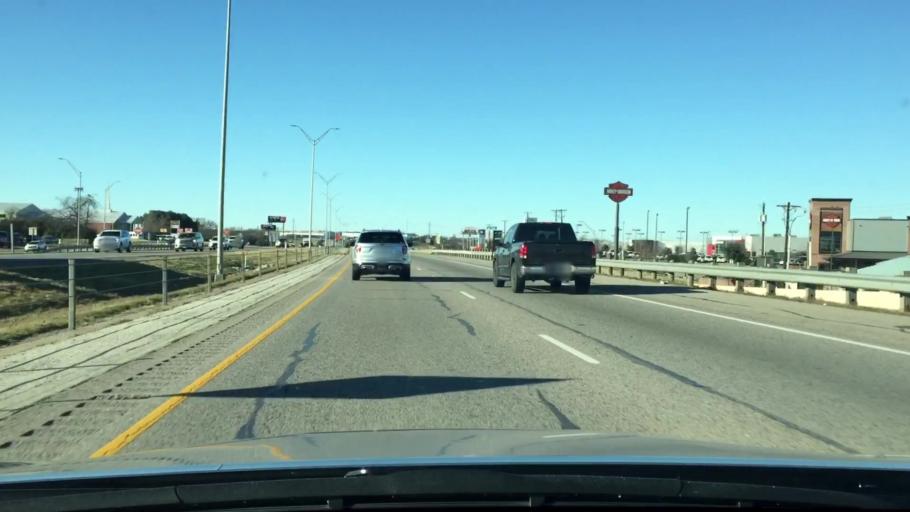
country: US
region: Texas
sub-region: Johnson County
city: Burleson
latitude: 32.5452
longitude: -97.3154
